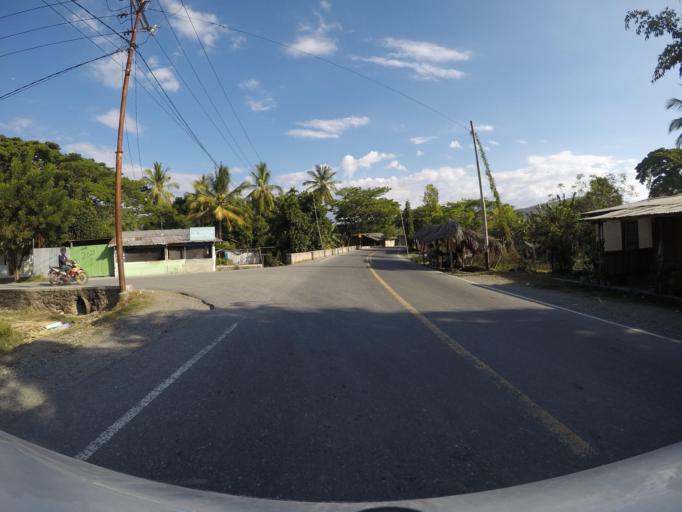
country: TL
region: Liquica
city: Maubara
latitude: -8.7372
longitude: 125.1367
